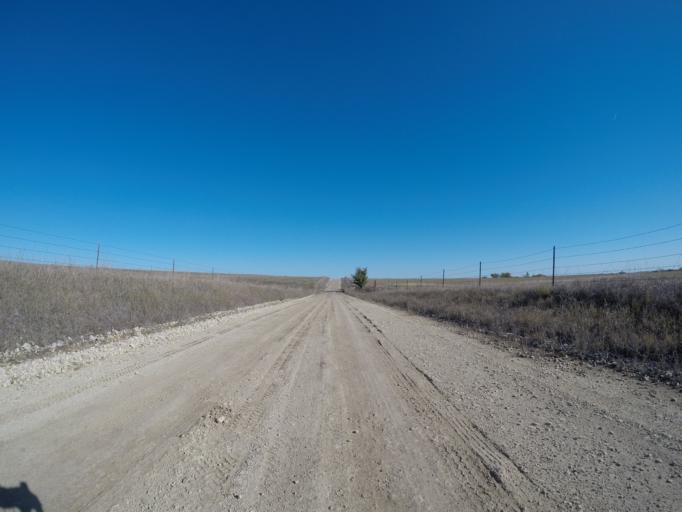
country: US
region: Kansas
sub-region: Wabaunsee County
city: Alma
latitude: 38.8860
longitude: -96.4013
